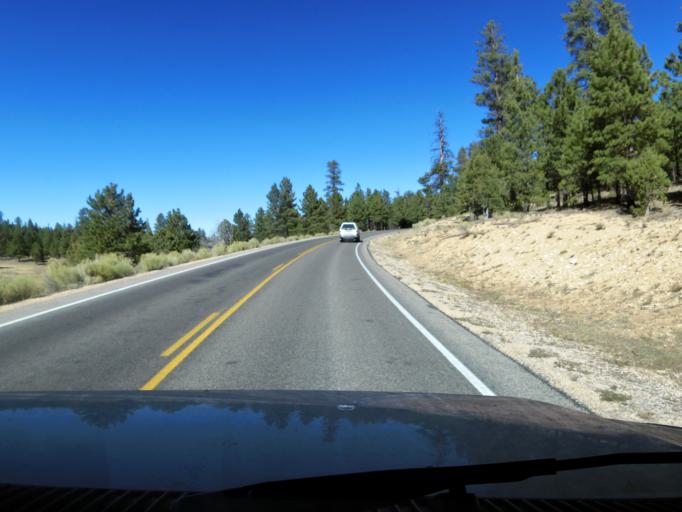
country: US
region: Utah
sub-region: Garfield County
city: Panguitch
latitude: 37.6018
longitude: -112.2078
